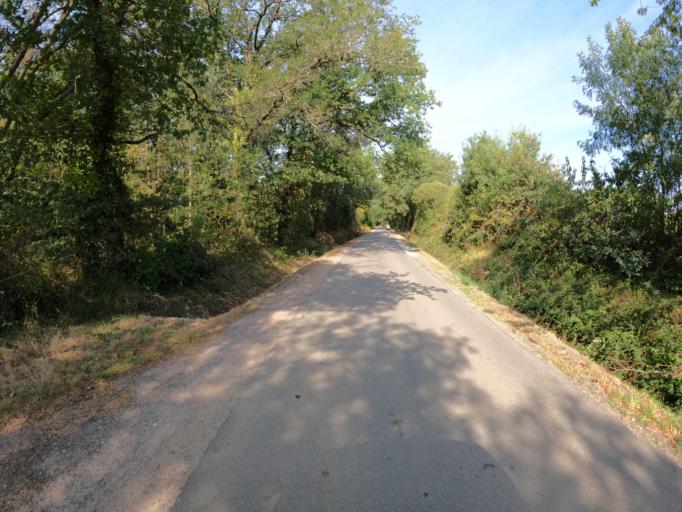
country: FR
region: Pays de la Loire
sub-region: Departement de la Vendee
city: Saint-Christophe-du-Ligneron
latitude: 46.8127
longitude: -1.8197
